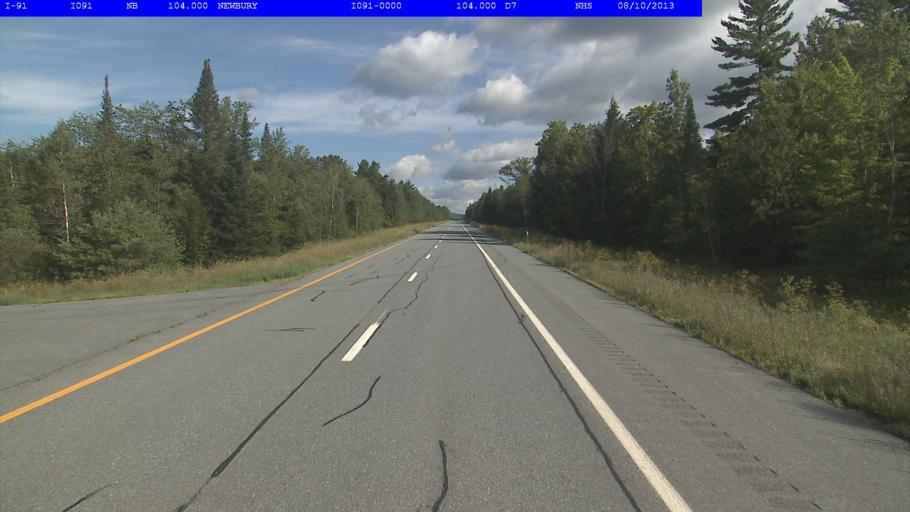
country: US
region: New Hampshire
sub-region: Grafton County
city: Haverhill
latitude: 44.0710
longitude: -72.1104
